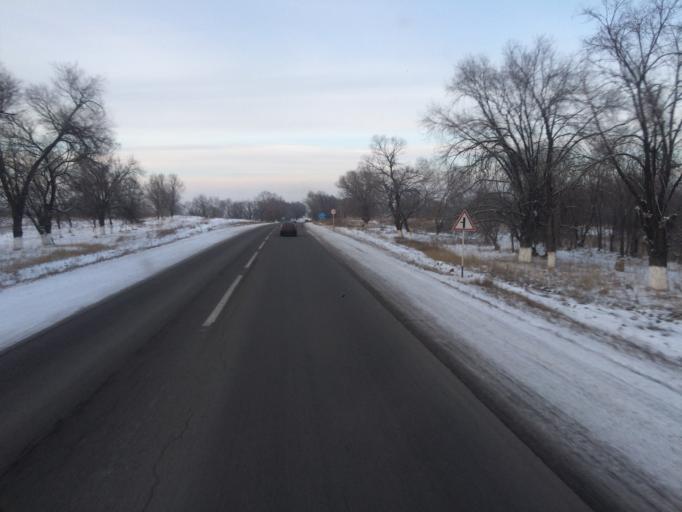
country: KZ
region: Almaty Oblysy
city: Burunday
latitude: 43.3246
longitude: 76.6629
